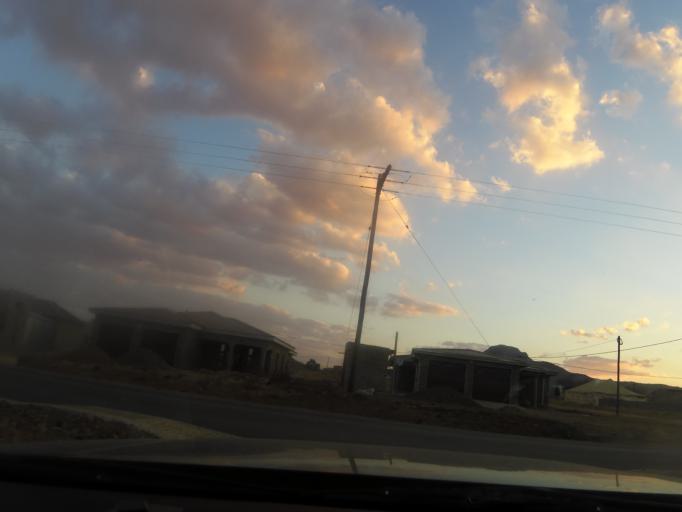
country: LS
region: Maseru
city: Maseru
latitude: -29.3670
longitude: 27.4762
